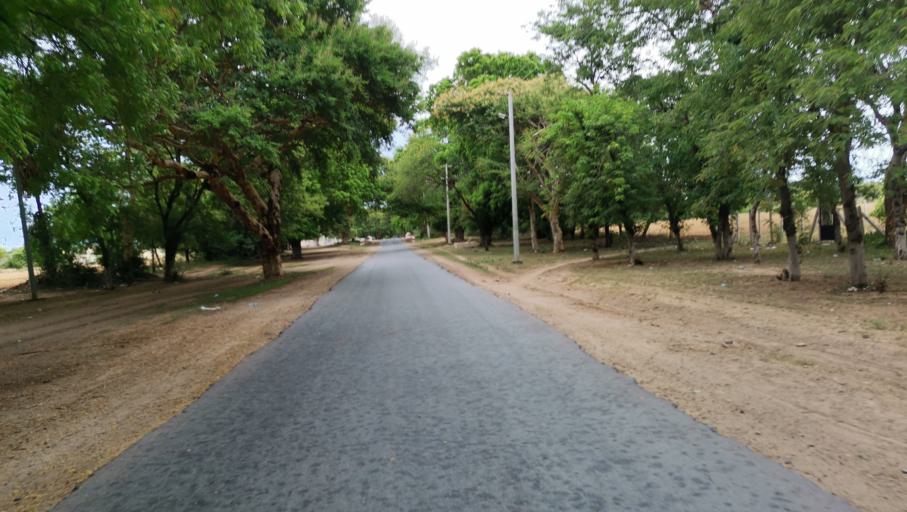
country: MM
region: Mandalay
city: Myingyan
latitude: 21.8458
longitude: 95.4287
